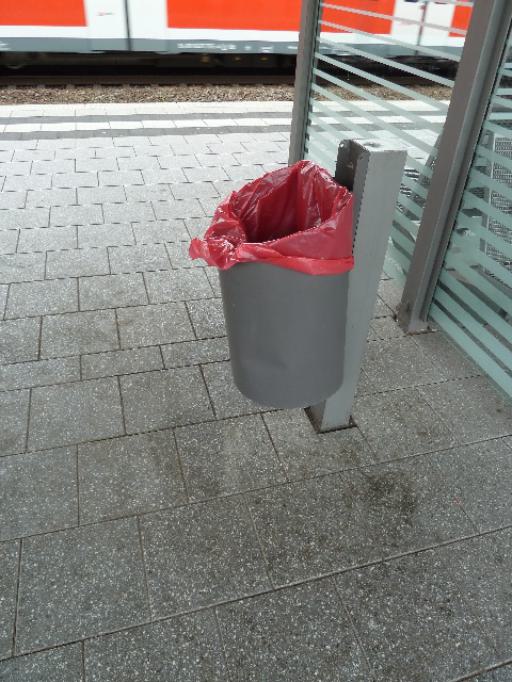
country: DE
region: Baden-Wuerttemberg
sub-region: Karlsruhe Region
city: Eberbach
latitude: 49.4660
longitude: 8.9835
